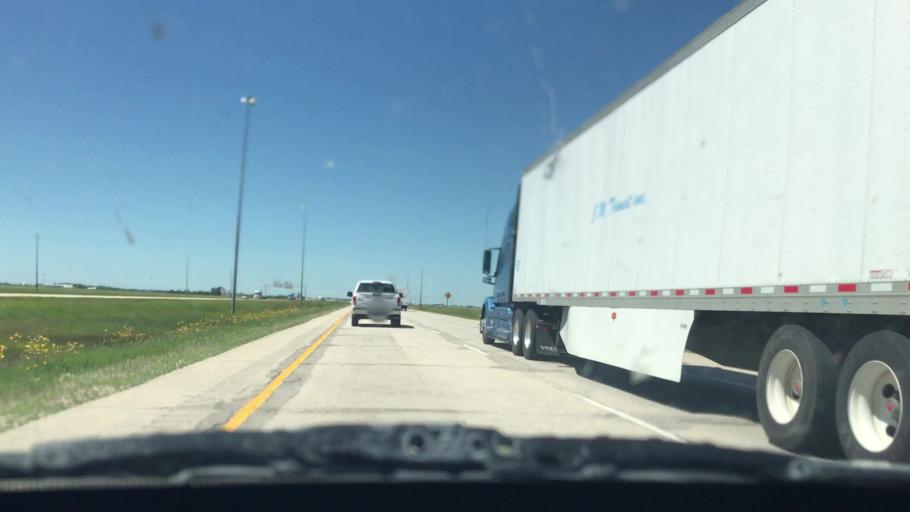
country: CA
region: Manitoba
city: Steinbach
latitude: 49.7021
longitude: -96.6485
